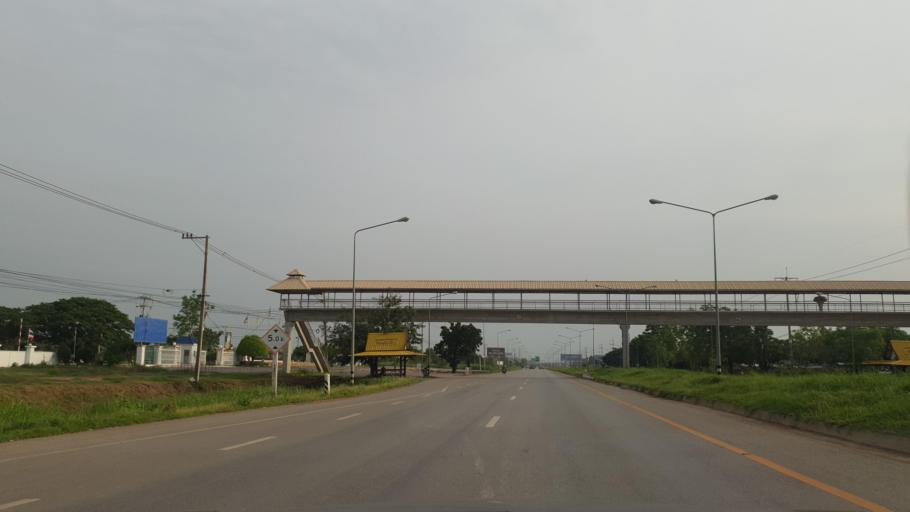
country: TH
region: Phitsanulok
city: Phitsanulok
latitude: 16.8036
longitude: 100.3316
